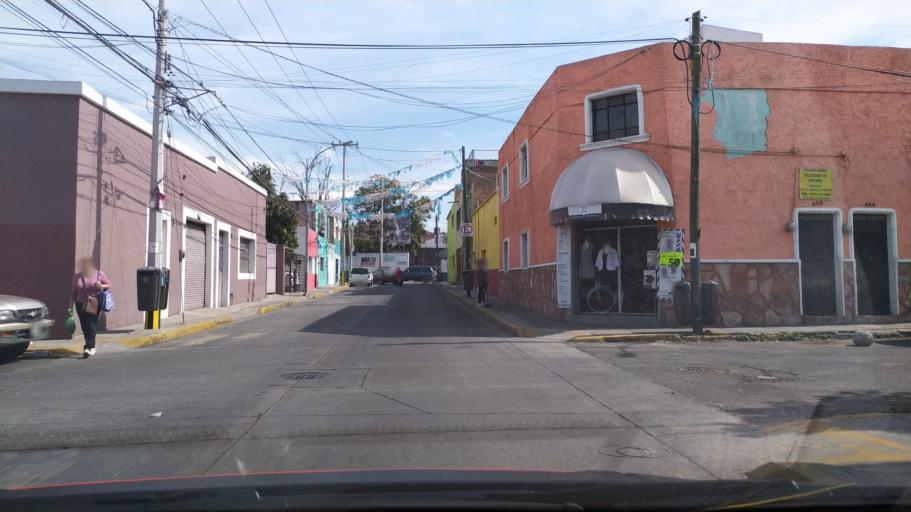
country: MX
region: Jalisco
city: Tlaquepaque
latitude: 20.6816
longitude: -103.3294
